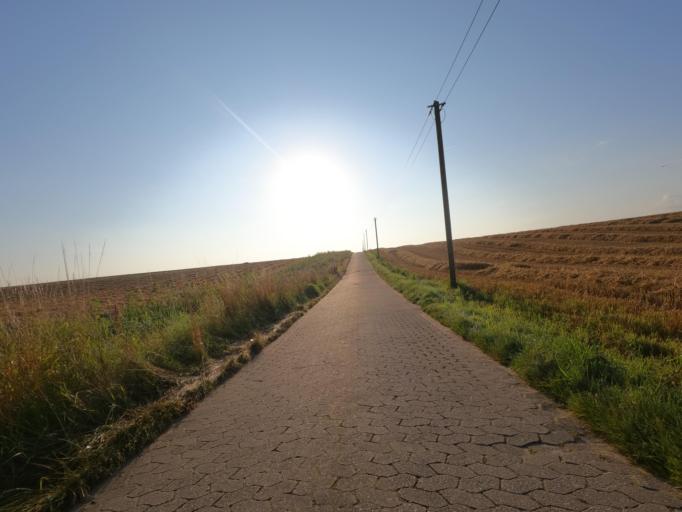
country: DE
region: North Rhine-Westphalia
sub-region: Regierungsbezirk Koln
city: Titz
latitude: 51.0175
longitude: 6.3750
